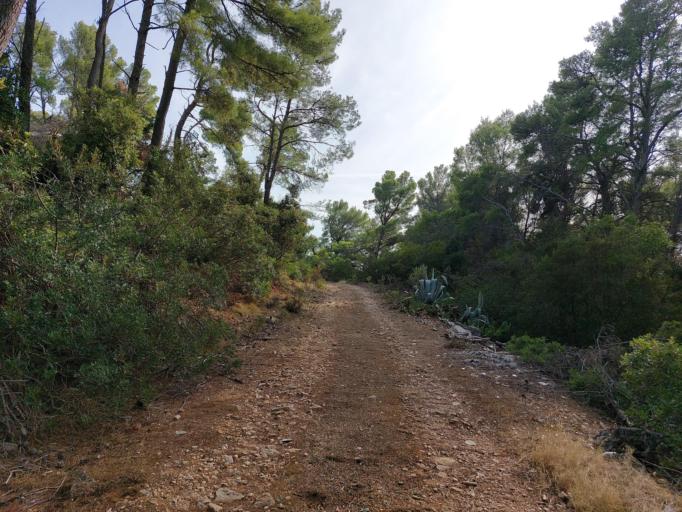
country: HR
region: Dubrovacko-Neretvanska
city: Smokvica
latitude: 42.7345
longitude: 16.8300
